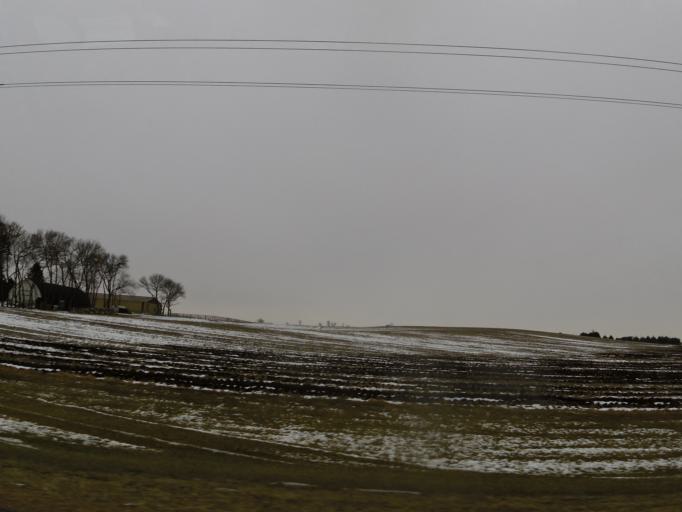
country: US
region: Minnesota
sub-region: Le Sueur County
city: New Prague
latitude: 44.6306
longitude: -93.5159
